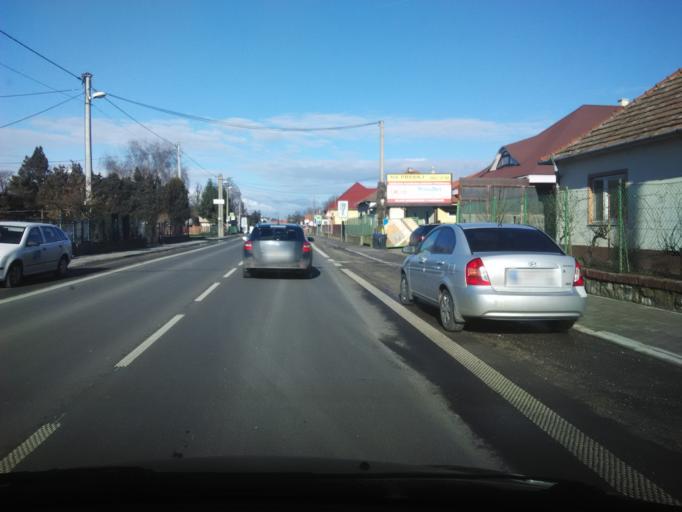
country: SK
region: Nitriansky
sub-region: Okres Nitra
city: Nitra
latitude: 48.2711
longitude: 18.1007
